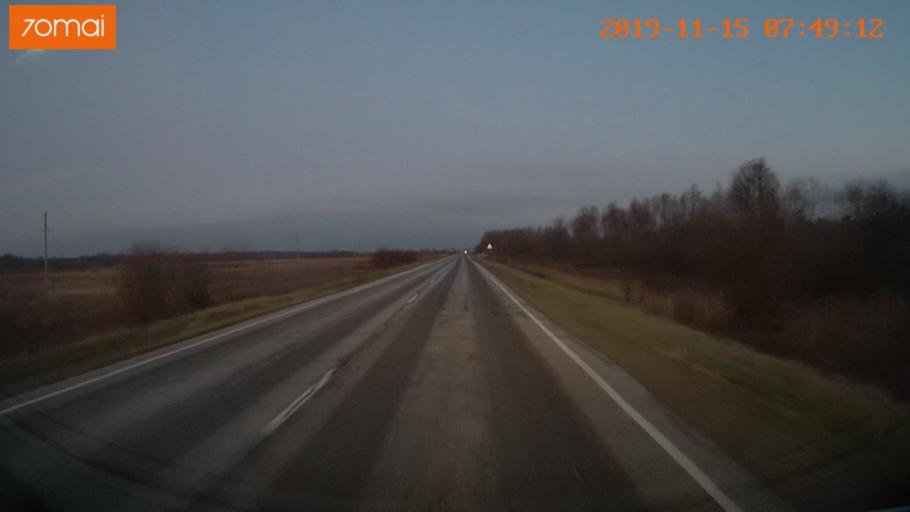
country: RU
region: Vologda
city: Cherepovets
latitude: 58.8586
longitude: 38.2335
